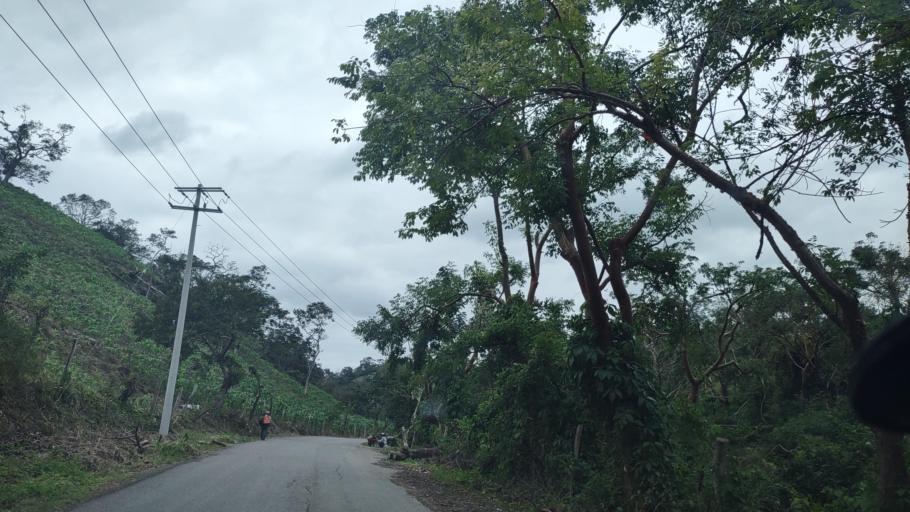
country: MX
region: Veracruz
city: Papantla de Olarte
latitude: 20.4447
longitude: -97.2974
